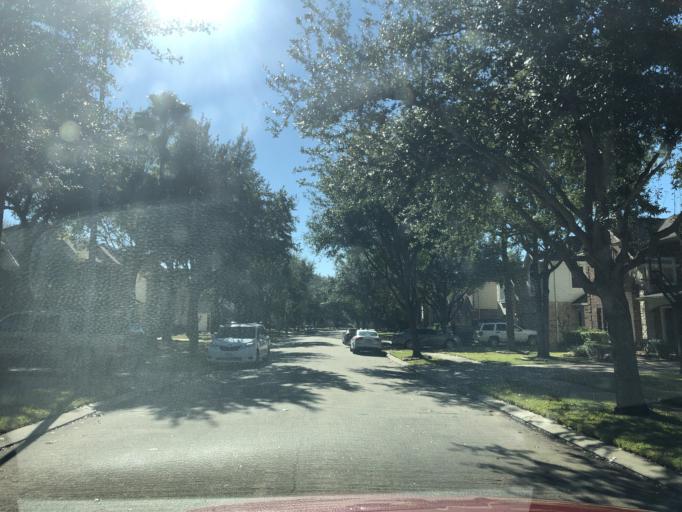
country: US
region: Texas
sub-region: Harris County
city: Oak Cliff Place
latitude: 29.9360
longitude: -95.6612
